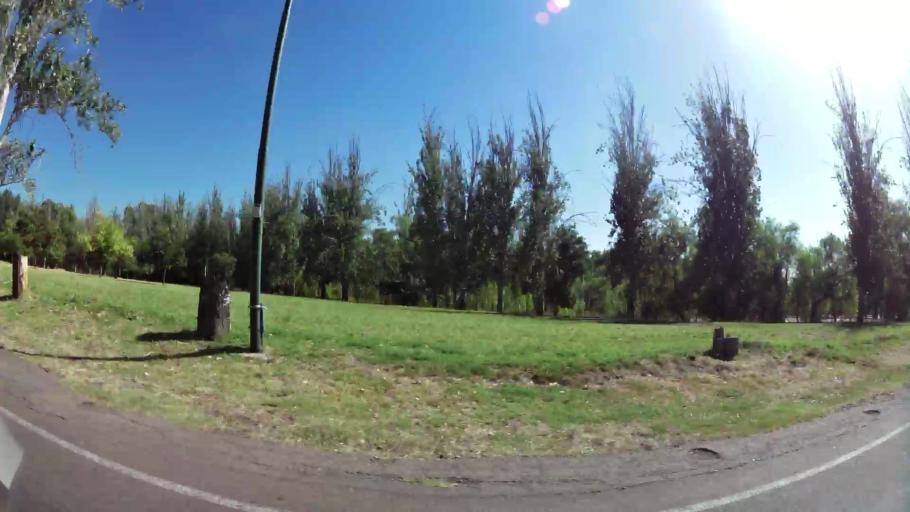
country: AR
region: Mendoza
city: Mendoza
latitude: -32.8925
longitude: -68.8814
